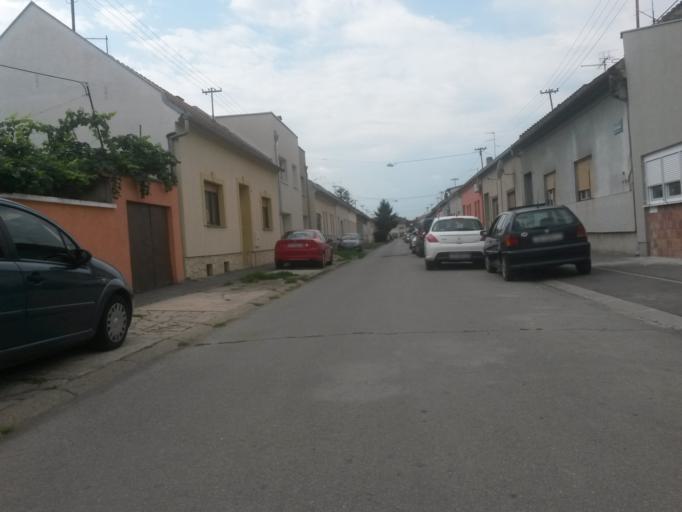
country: HR
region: Osjecko-Baranjska
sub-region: Grad Osijek
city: Osijek
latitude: 45.5484
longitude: 18.6819
